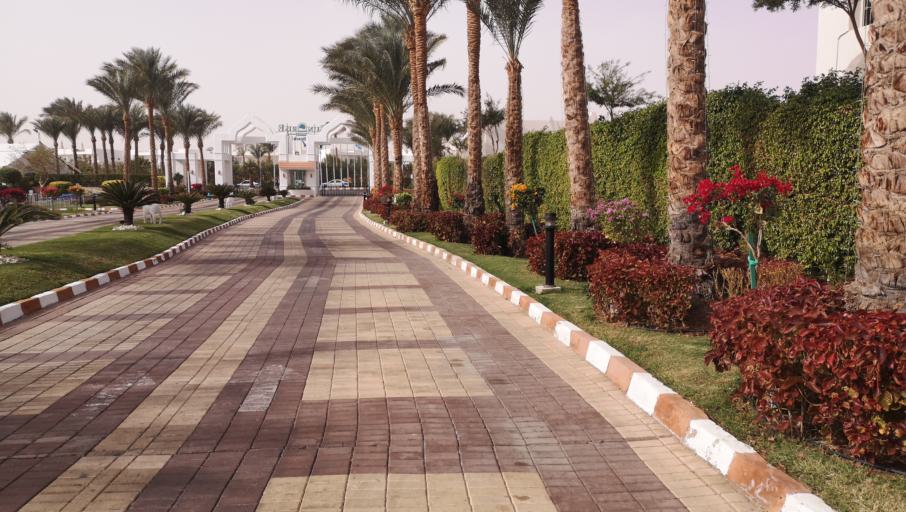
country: EG
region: South Sinai
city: Sharm el-Sheikh
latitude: 27.8646
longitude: 34.3173
